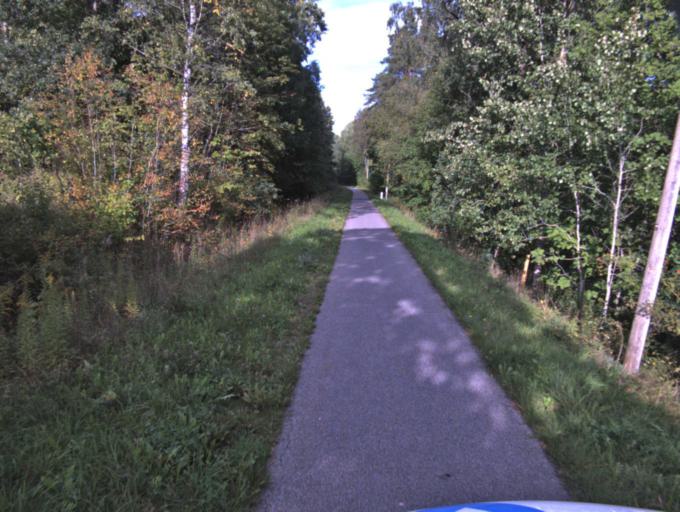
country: SE
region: Vaestra Goetaland
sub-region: Ulricehamns Kommun
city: Ulricehamn
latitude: 57.9040
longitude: 13.4691
